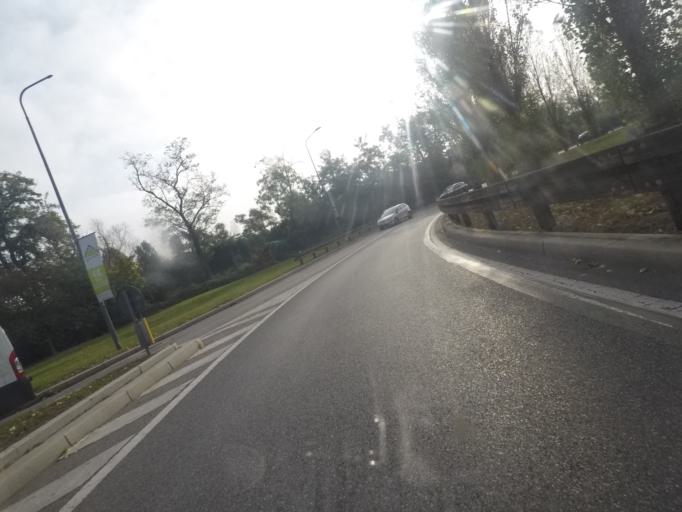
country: IT
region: Lombardy
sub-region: Citta metropolitana di Milano
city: Cologno Monzese
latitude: 45.5141
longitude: 9.2677
